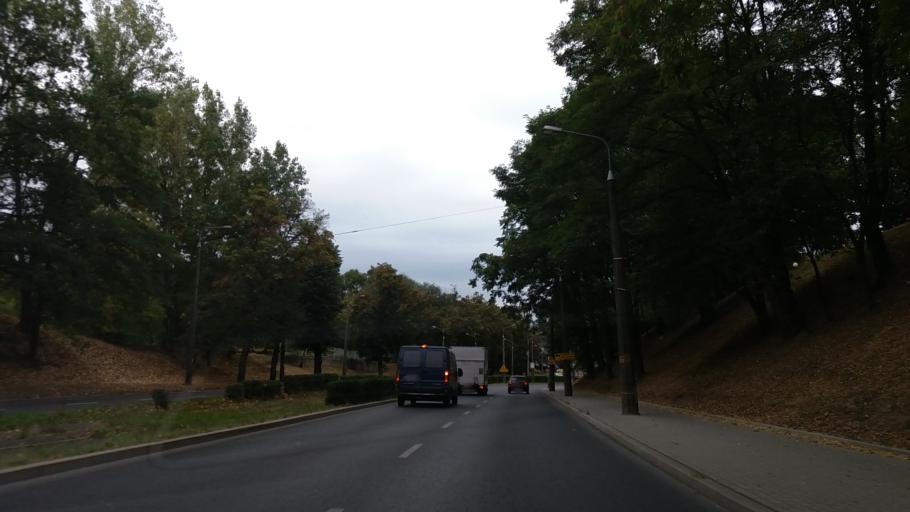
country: PL
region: Lubusz
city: Gorzow Wielkopolski
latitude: 52.7401
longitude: 15.2560
